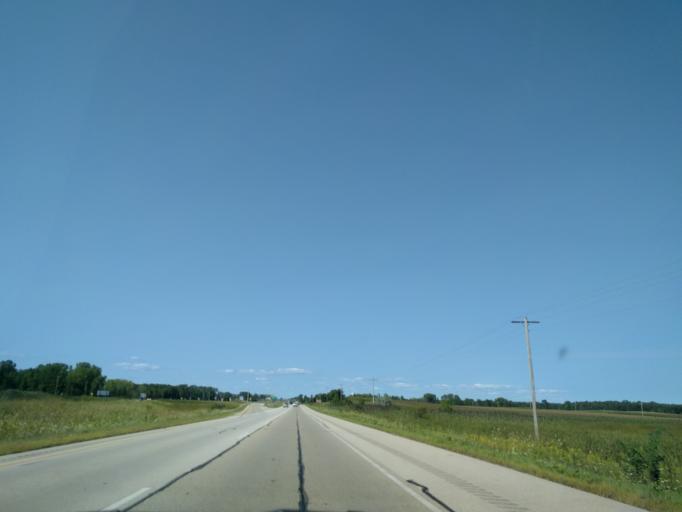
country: US
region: Wisconsin
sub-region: Brown County
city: Suamico
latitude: 44.7360
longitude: -88.0506
